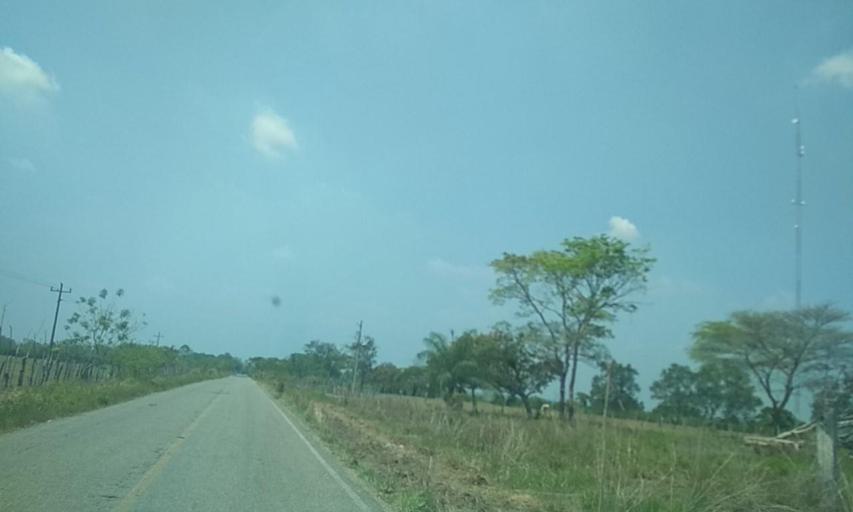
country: MX
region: Tabasco
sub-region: Huimanguillo
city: Paso de la Mina 3ra. Seccion
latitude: 17.8374
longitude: -93.6157
